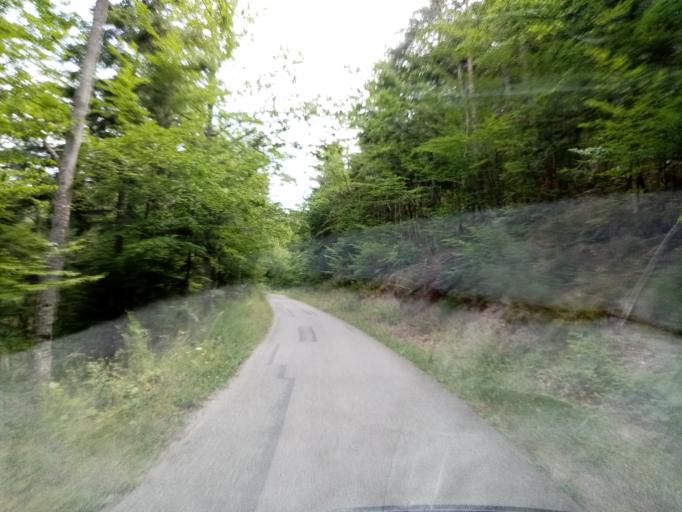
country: FR
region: Alsace
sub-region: Departement du Bas-Rhin
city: Ville
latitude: 48.3537
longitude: 7.3390
